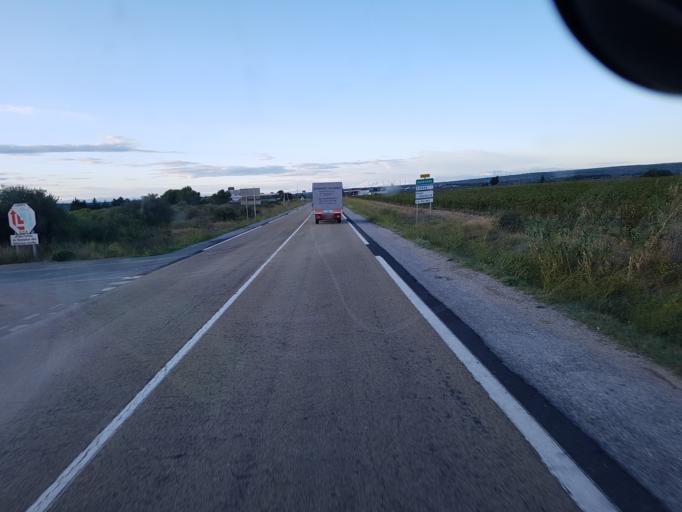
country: FR
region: Languedoc-Roussillon
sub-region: Departement de l'Aude
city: Leucate
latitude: 42.9408
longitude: 2.9900
